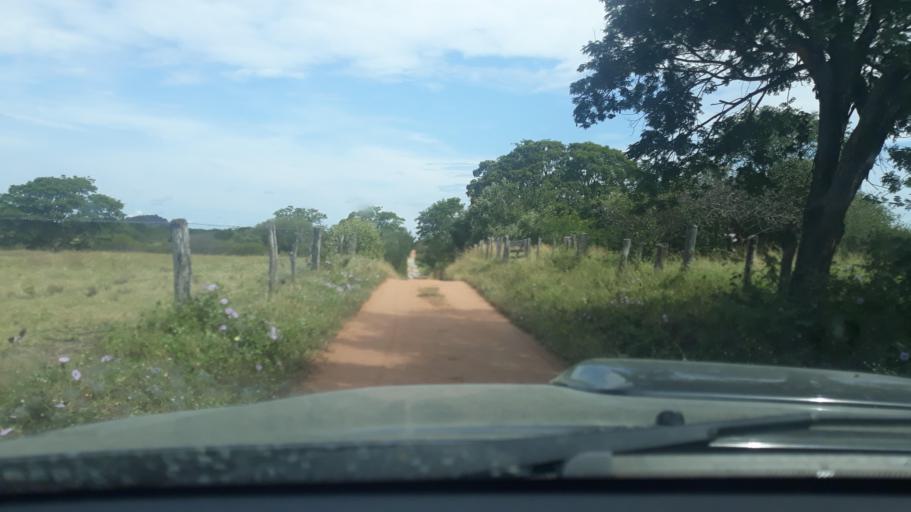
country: BR
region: Bahia
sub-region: Riacho De Santana
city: Riacho de Santana
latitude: -13.8600
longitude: -43.0345
